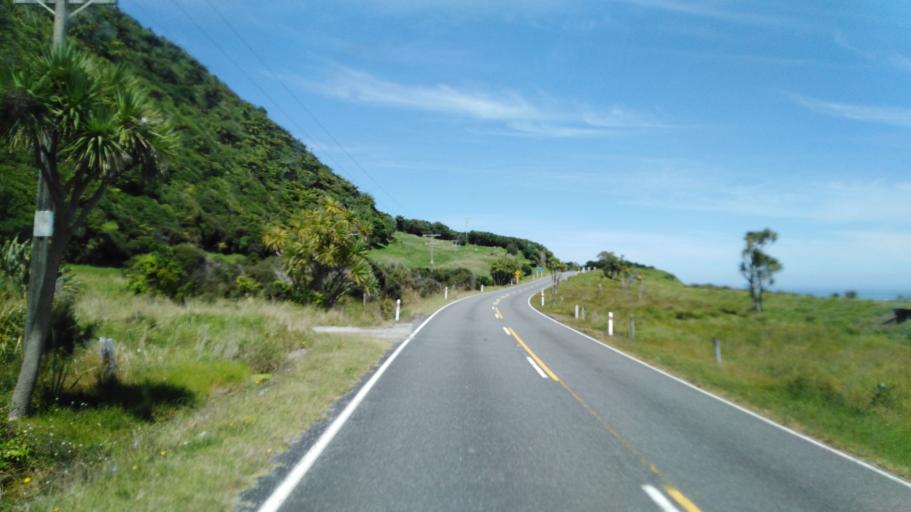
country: NZ
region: West Coast
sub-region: Buller District
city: Westport
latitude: -41.5888
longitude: 171.8929
